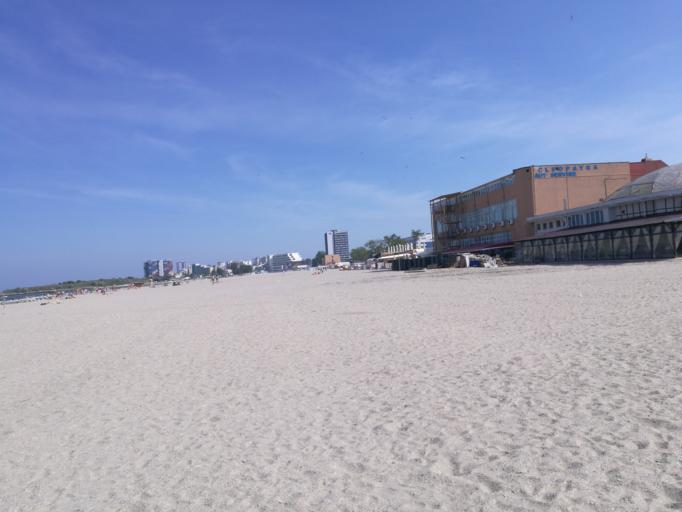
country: RO
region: Constanta
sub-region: Municipiul Constanta
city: Palazu Mare
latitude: 44.2236
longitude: 28.6333
